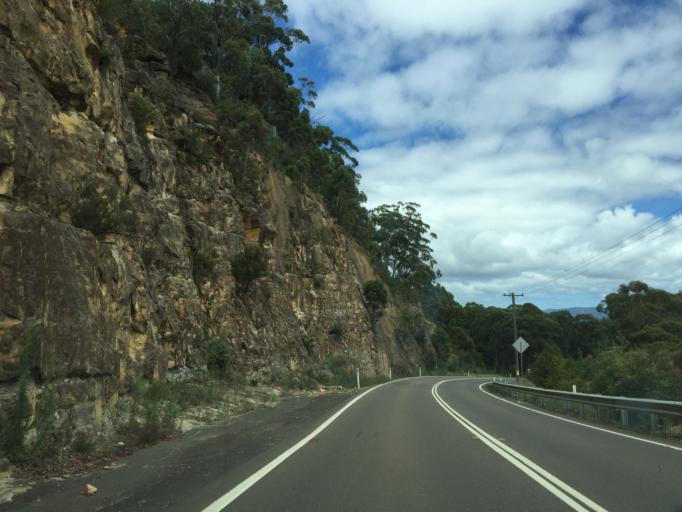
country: AU
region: New South Wales
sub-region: Hawkesbury
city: Richmond
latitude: -33.5192
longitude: 150.6201
